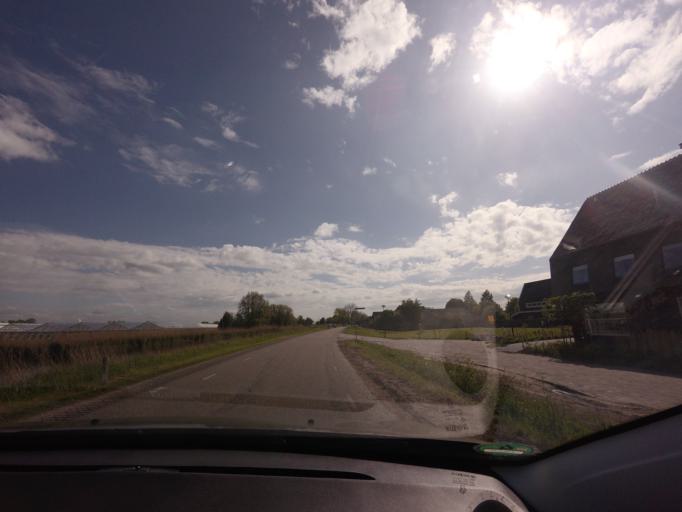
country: NL
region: North Holland
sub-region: Gemeente Heerhugowaard
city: Heerhugowaard
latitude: 52.6664
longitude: 4.8697
